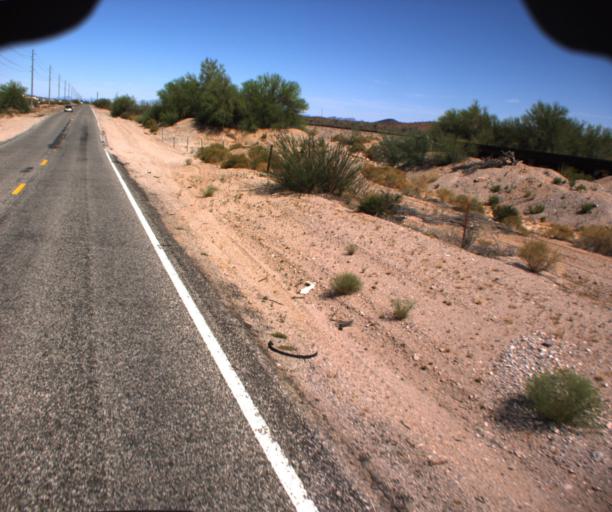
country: US
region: Arizona
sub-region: La Paz County
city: Quartzsite
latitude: 33.9011
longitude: -113.9739
